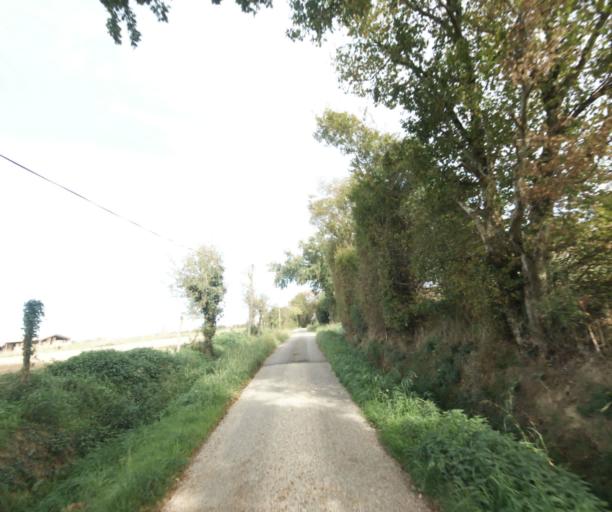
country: FR
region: Midi-Pyrenees
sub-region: Departement du Gers
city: Eauze
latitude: 43.8780
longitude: 0.1207
